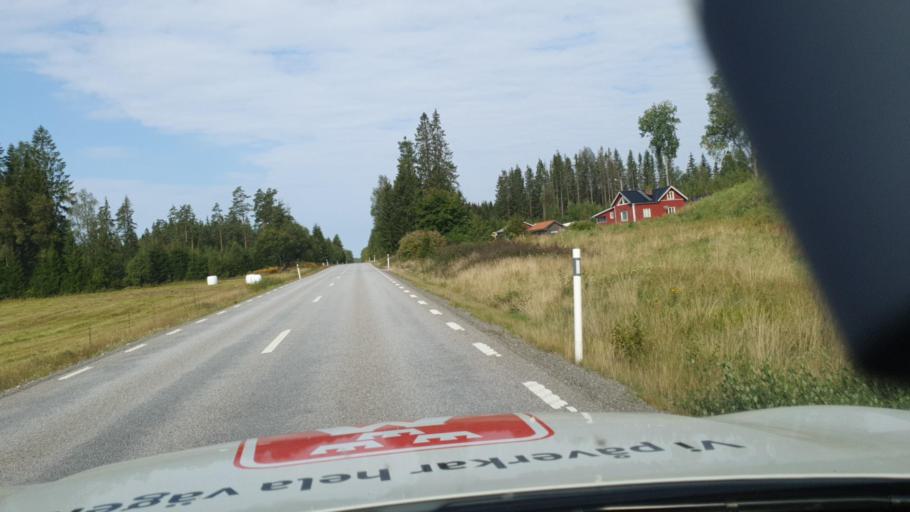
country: SE
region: Vaestra Goetaland
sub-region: Dals-Ed Kommun
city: Ed
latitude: 58.8723
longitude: 12.0112
